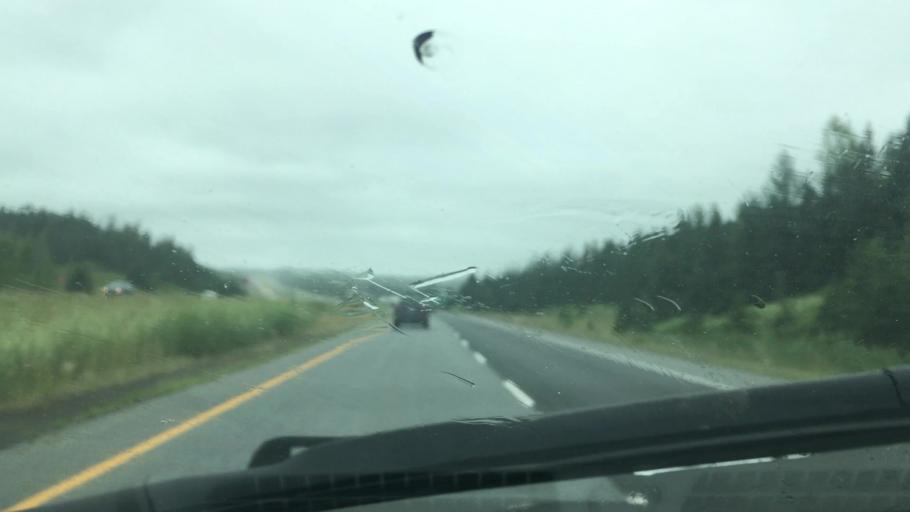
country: CA
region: Nova Scotia
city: Truro
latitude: 45.2436
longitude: -63.2925
